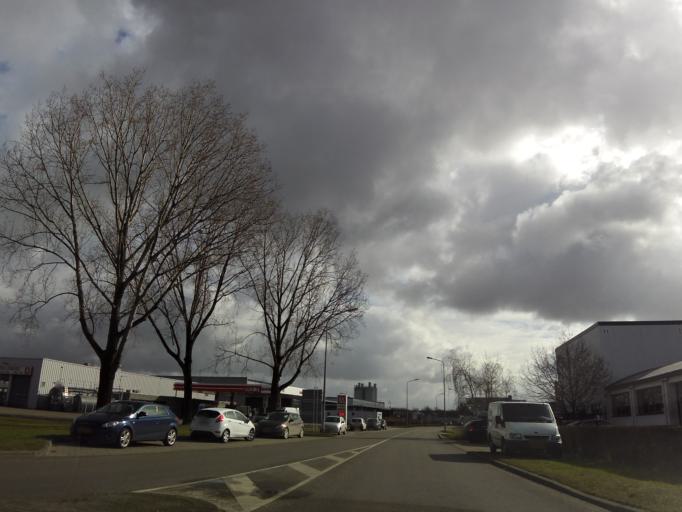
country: NL
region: Limburg
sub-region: Gemeente Maastricht
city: Maastricht
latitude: 50.8766
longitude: 5.7044
